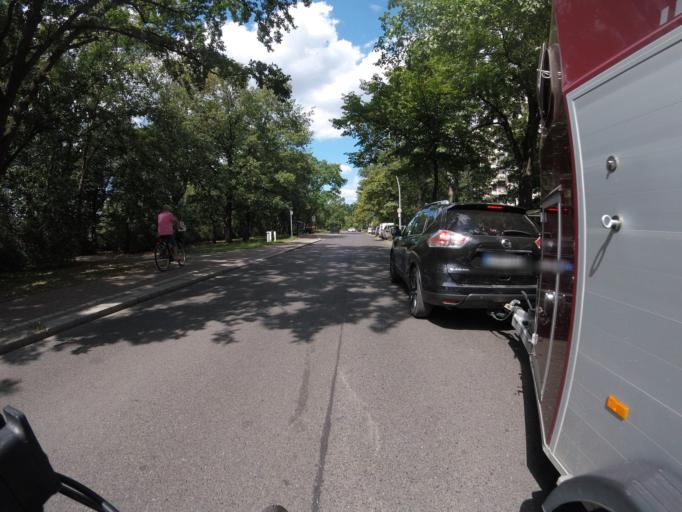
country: DE
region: Berlin
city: Siemensstadt
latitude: 52.5468
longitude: 13.2596
